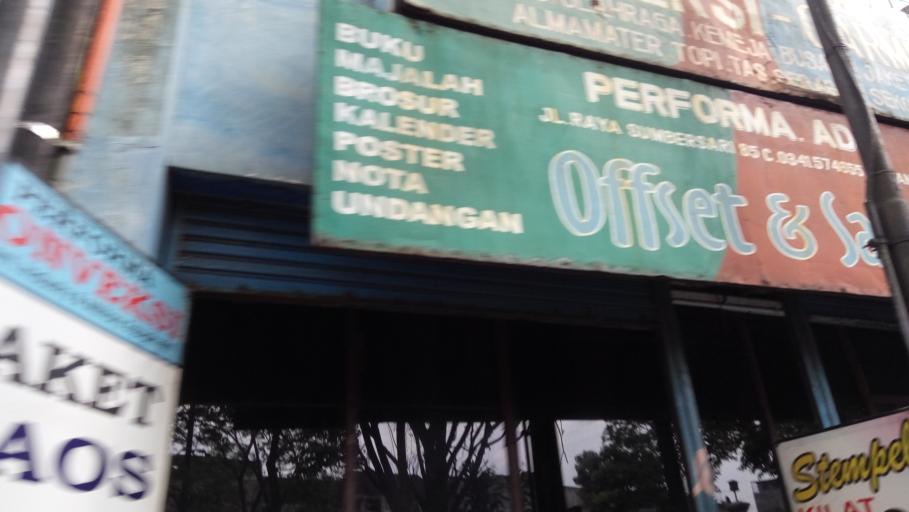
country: ID
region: East Java
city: Malang
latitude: -7.9523
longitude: 112.6093
